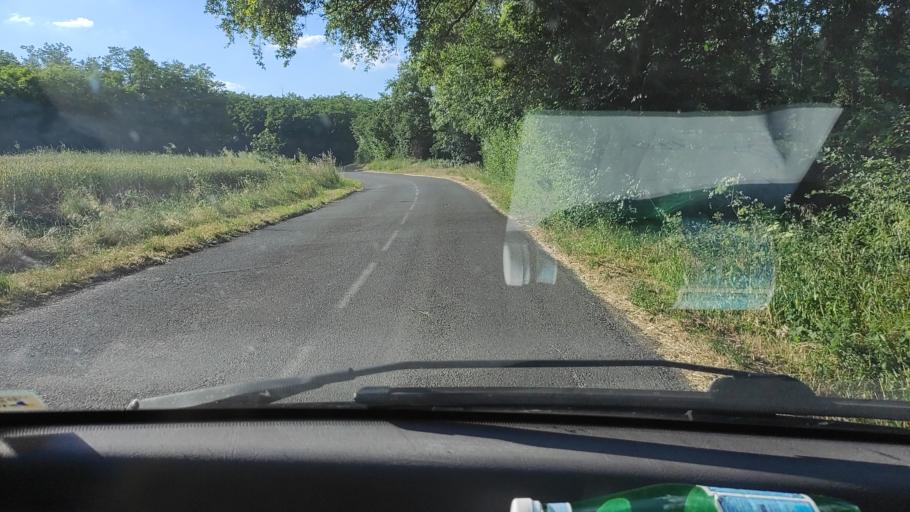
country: FR
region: Poitou-Charentes
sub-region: Departement des Deux-Sevres
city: Saint-Varent
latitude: 46.8589
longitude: -0.2028
